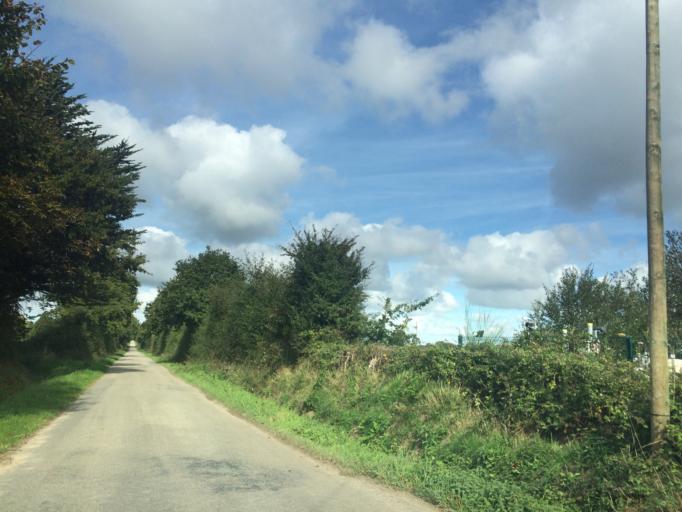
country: FR
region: Pays de la Loire
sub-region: Departement de la Loire-Atlantique
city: Chemere
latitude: 47.1308
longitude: -1.8968
